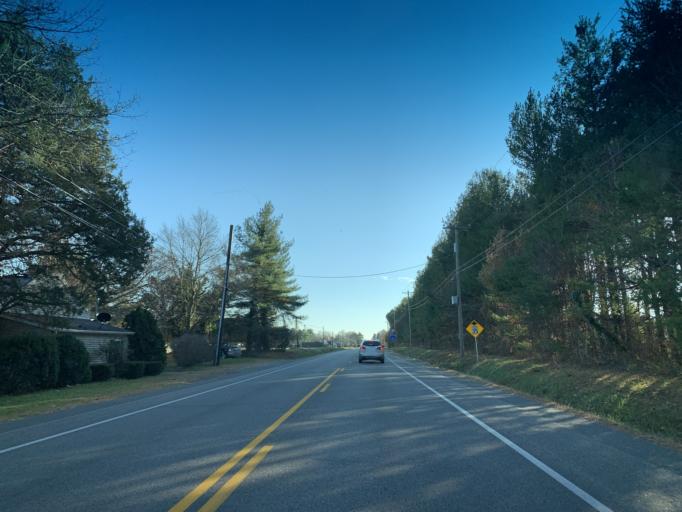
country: US
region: Delaware
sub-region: New Castle County
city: Middletown
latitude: 39.3530
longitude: -75.8774
